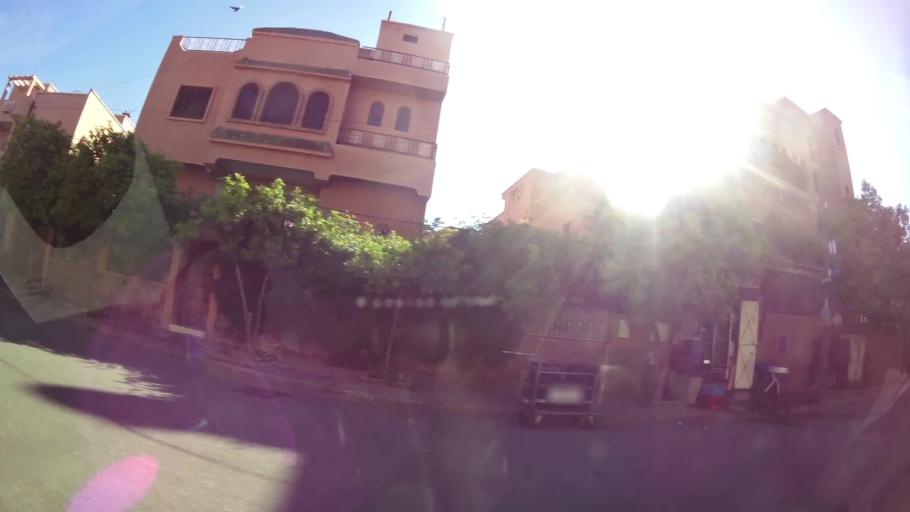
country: MA
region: Marrakech-Tensift-Al Haouz
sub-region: Marrakech
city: Marrakesh
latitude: 31.6472
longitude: -8.0139
